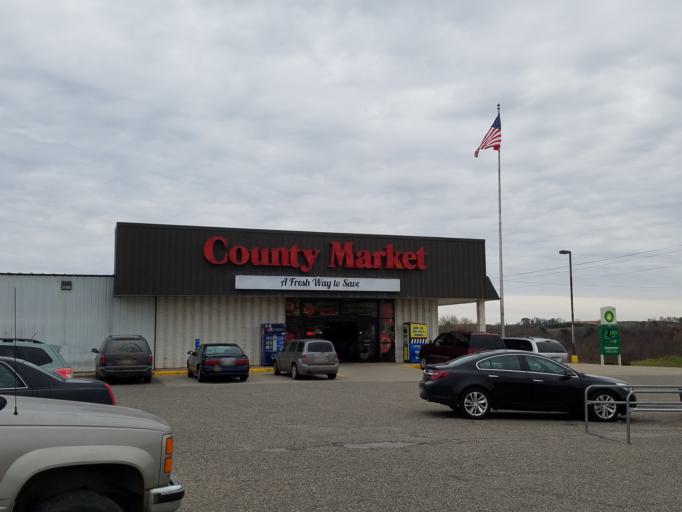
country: US
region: Wisconsin
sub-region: Vernon County
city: Hillsboro
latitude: 43.6610
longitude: -90.3283
